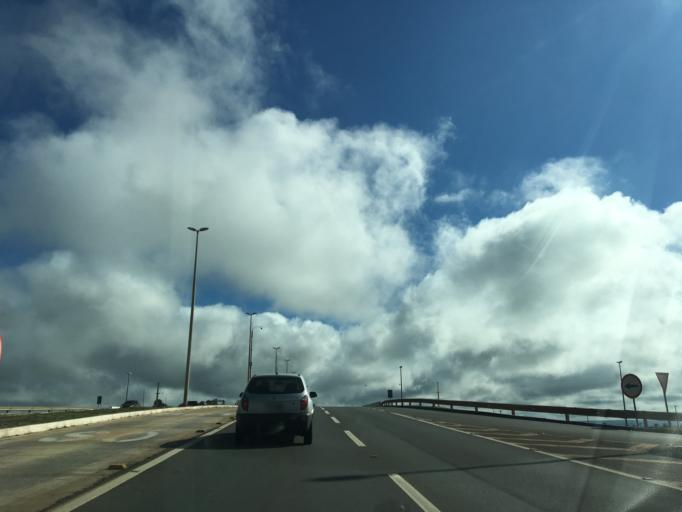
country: BR
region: Federal District
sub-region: Brasilia
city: Brasilia
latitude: -15.9670
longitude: -48.0216
